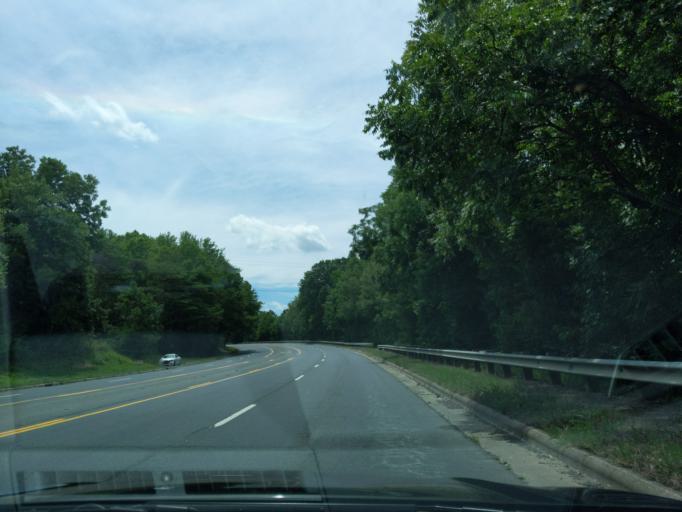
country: US
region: North Carolina
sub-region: Stanly County
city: Albemarle
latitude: 35.4420
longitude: -80.2217
